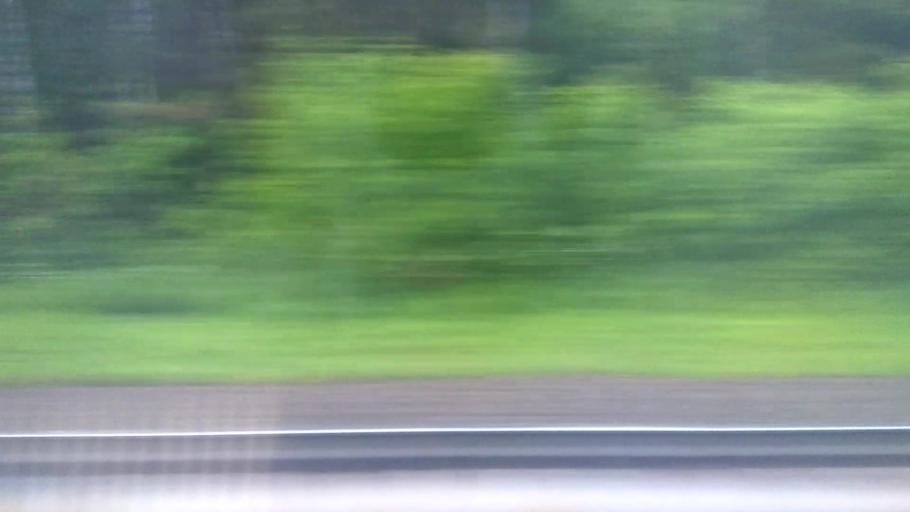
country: RU
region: Moskovskaya
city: Vostryakovo
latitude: 55.3645
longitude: 37.8280
